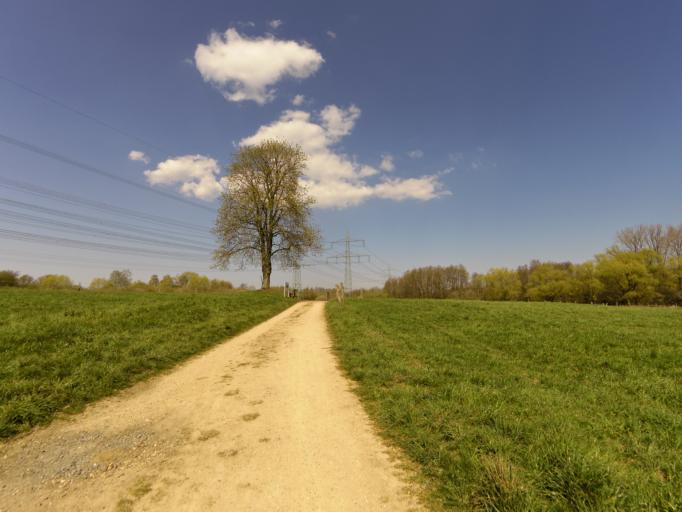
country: DE
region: North Rhine-Westphalia
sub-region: Regierungsbezirk Koln
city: Alfter
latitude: 50.6790
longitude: 7.0107
